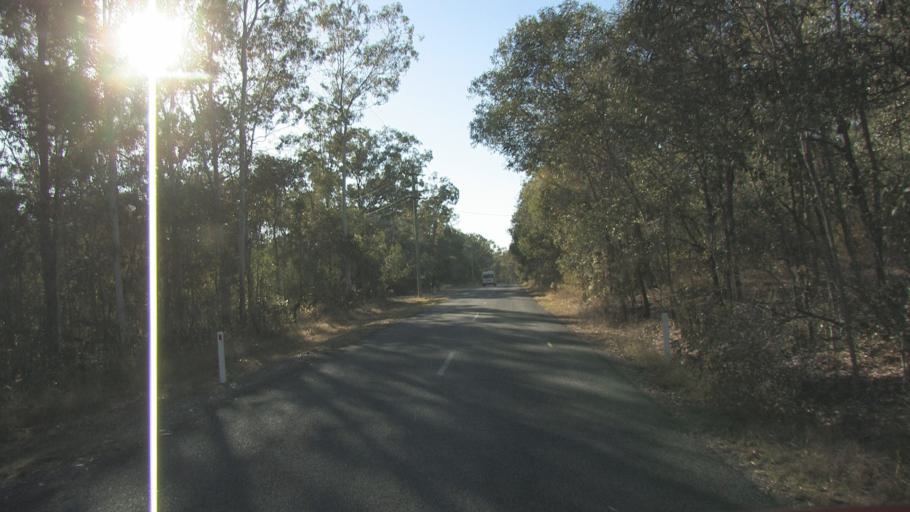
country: AU
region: Queensland
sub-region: Logan
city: North Maclean
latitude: -27.7839
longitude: 152.9650
